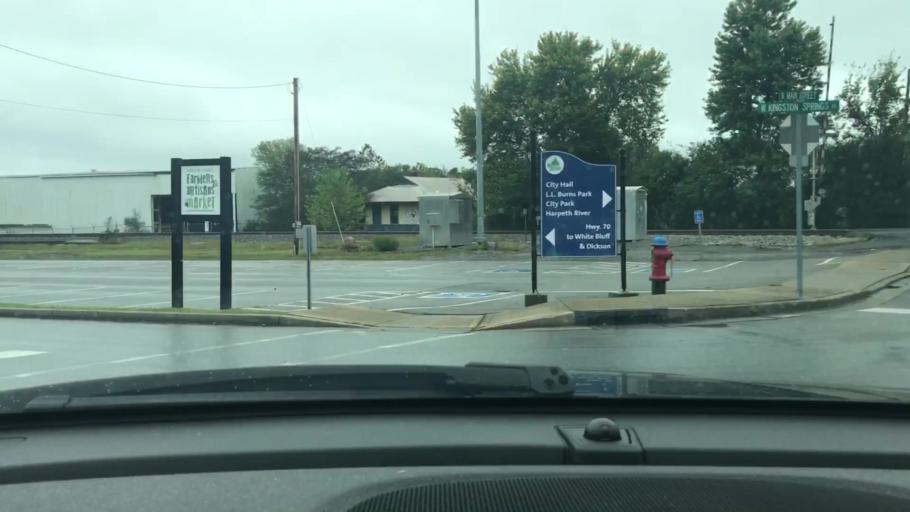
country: US
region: Tennessee
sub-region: Cheatham County
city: Kingston Springs
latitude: 36.1016
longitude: -87.1148
